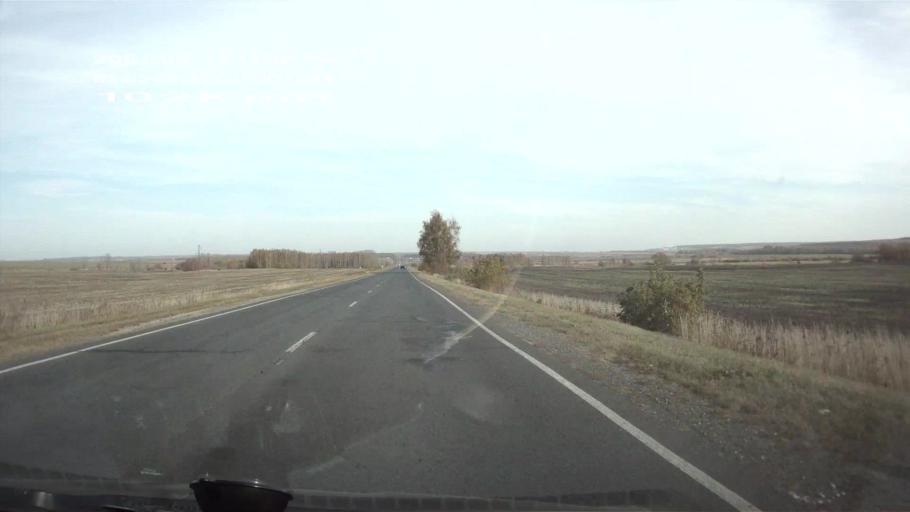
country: RU
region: Mordoviya
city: Atyashevo
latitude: 54.5401
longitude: 45.9341
